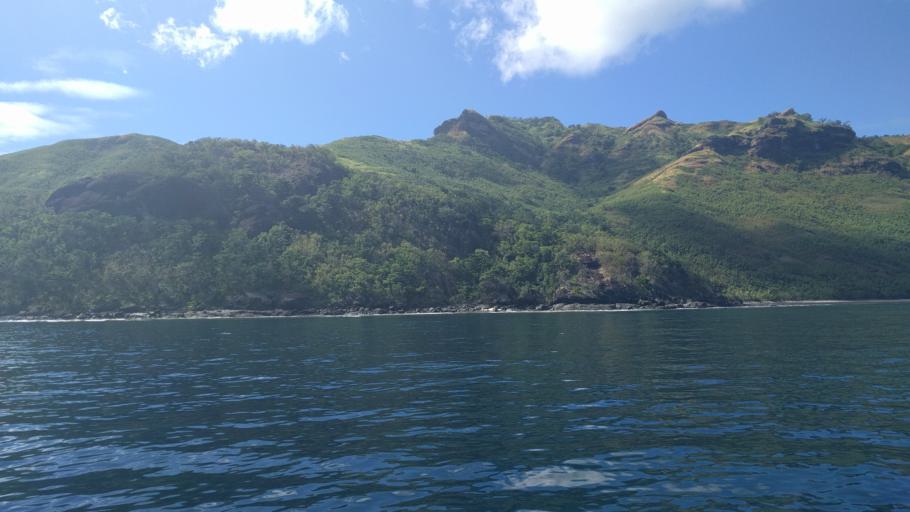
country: FJ
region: Western
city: Lautoka
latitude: -17.2903
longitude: 177.1005
